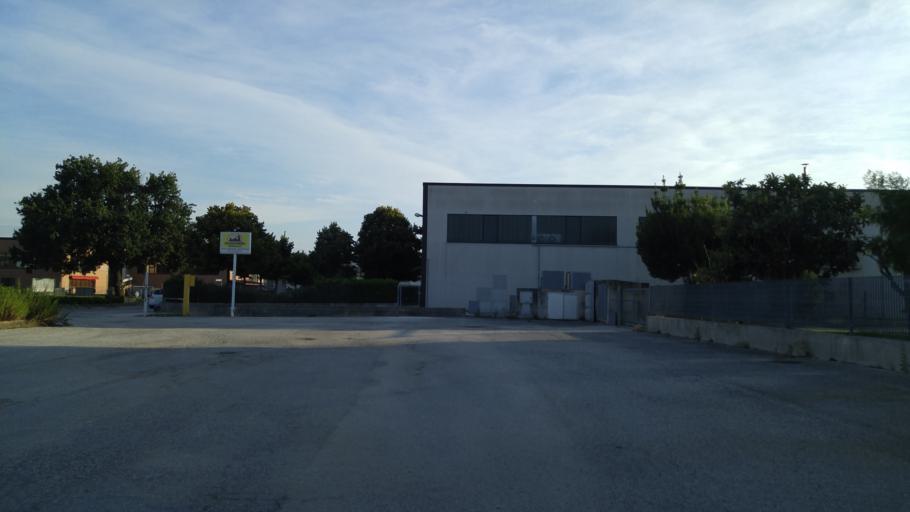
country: IT
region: The Marches
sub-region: Provincia di Pesaro e Urbino
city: Lucrezia
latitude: 43.7640
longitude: 12.9331
